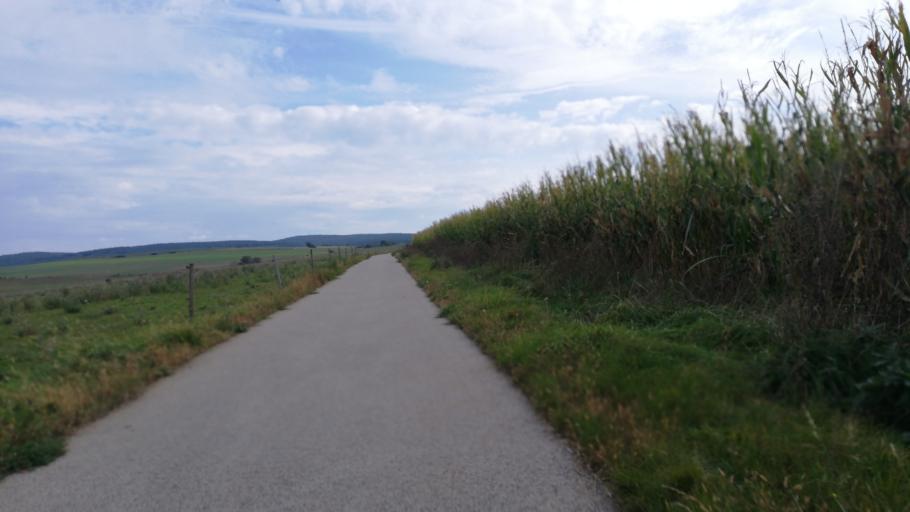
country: CZ
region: South Moravian
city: Sudomerice
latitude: 48.8481
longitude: 17.2702
